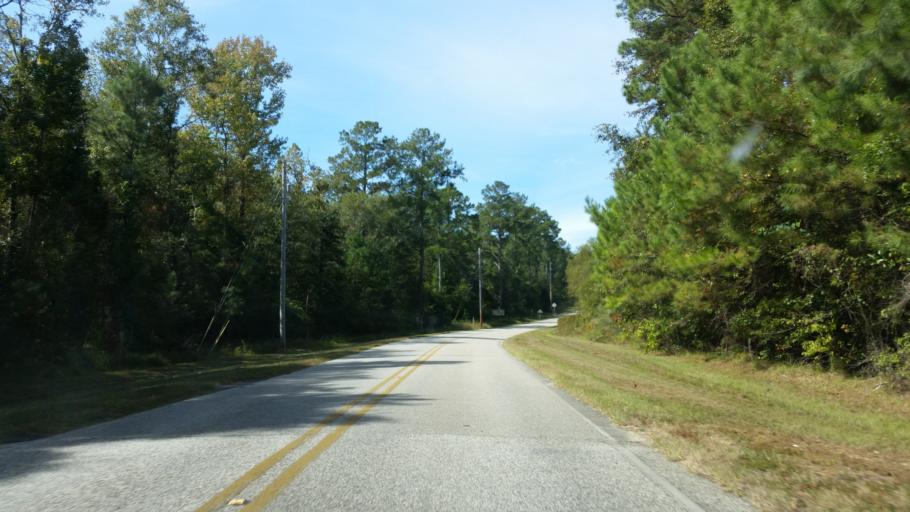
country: US
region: Alabama
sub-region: Baldwin County
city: Spanish Fort
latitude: 30.7401
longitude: -87.8764
